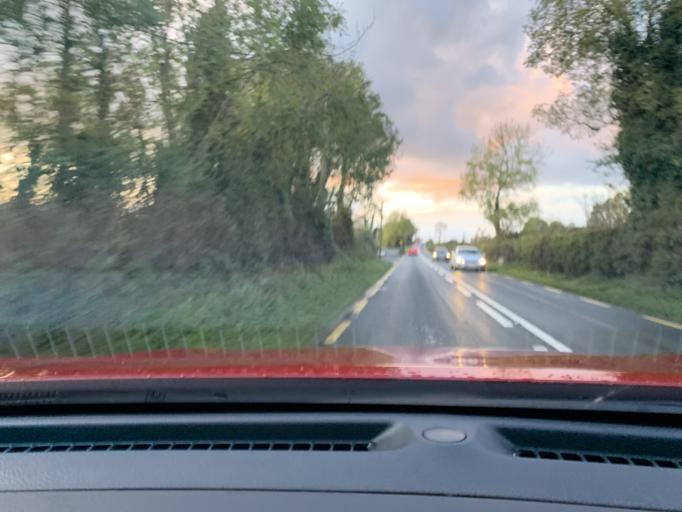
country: IE
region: Connaught
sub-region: Sligo
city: Ballymote
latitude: 54.1141
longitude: -8.4232
